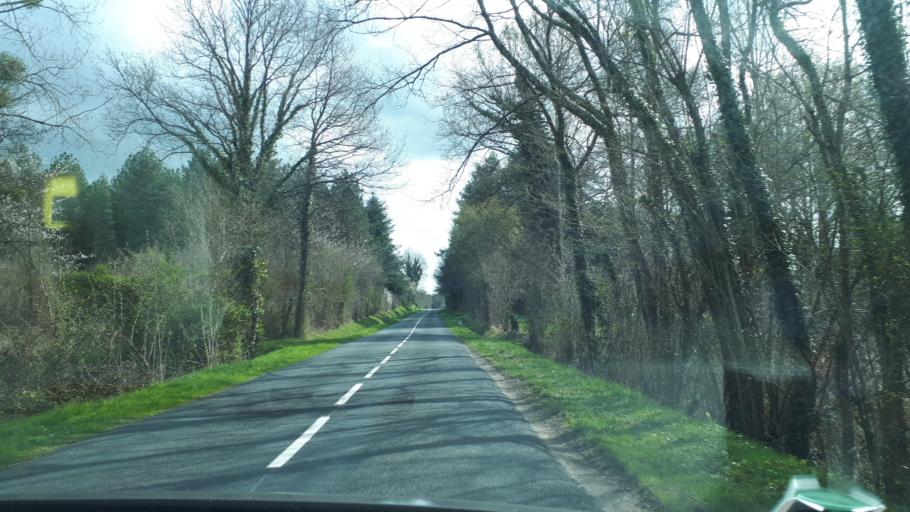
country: FR
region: Pays de la Loire
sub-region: Departement de la Sarthe
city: Challes
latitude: 47.8720
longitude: 0.3897
